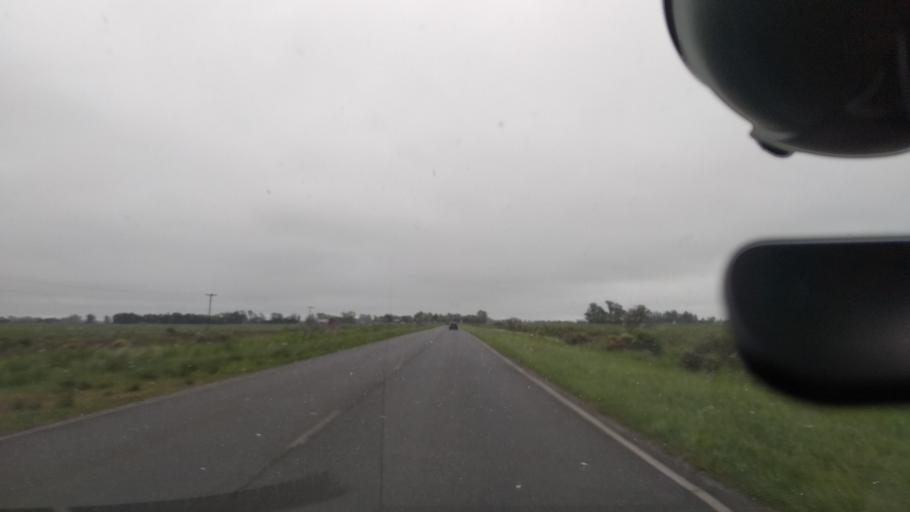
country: AR
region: Buenos Aires
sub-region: Partido de Magdalena
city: Magdalena
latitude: -35.2324
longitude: -57.7057
